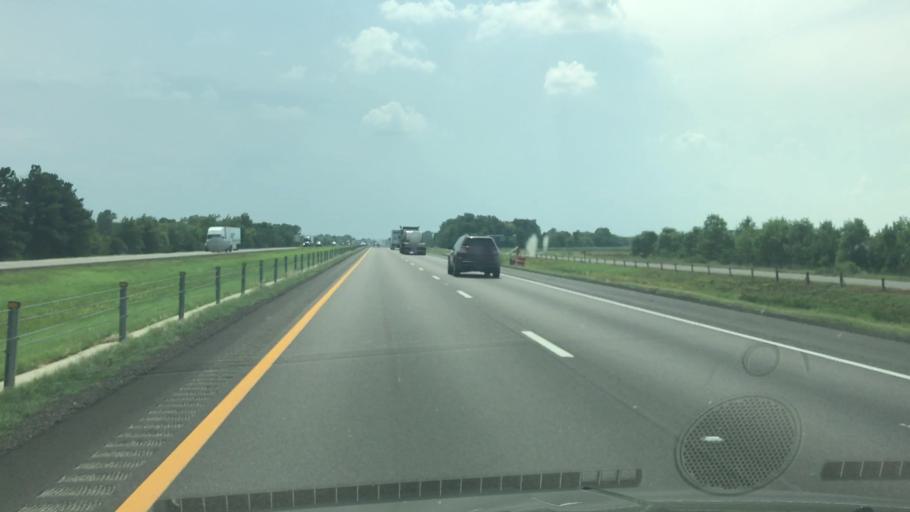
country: US
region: Arkansas
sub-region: Crittenden County
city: Earle
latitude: 35.1453
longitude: -90.4148
